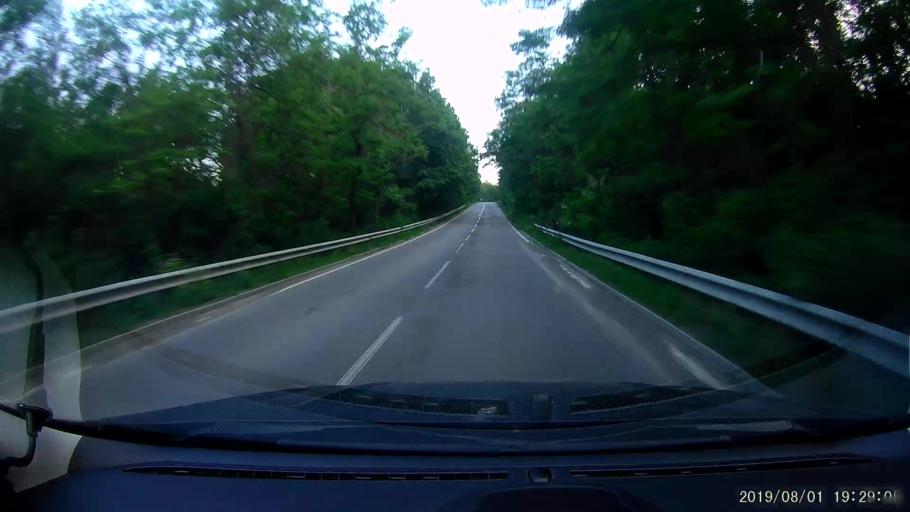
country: BG
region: Burgas
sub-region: Obshtina Sungurlare
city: Sungurlare
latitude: 42.8319
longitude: 26.9108
